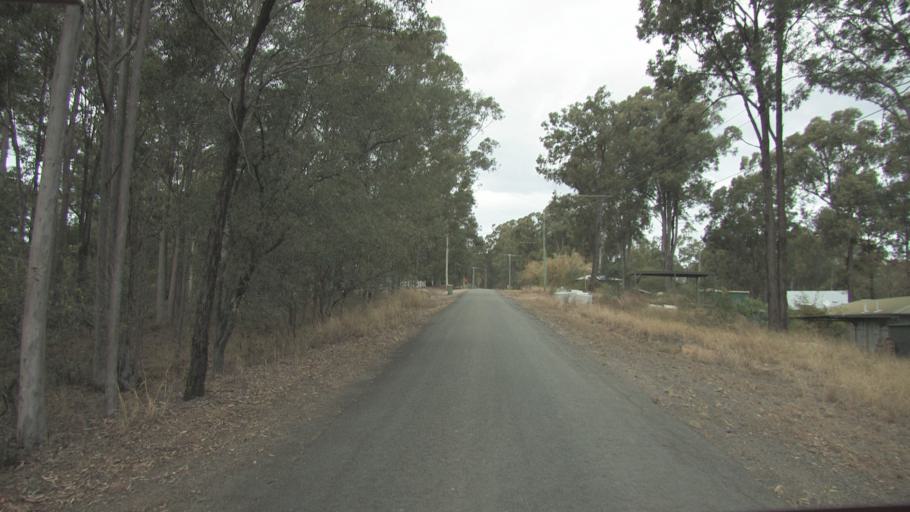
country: AU
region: Queensland
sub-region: Logan
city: Cedar Vale
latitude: -27.8955
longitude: 153.0252
